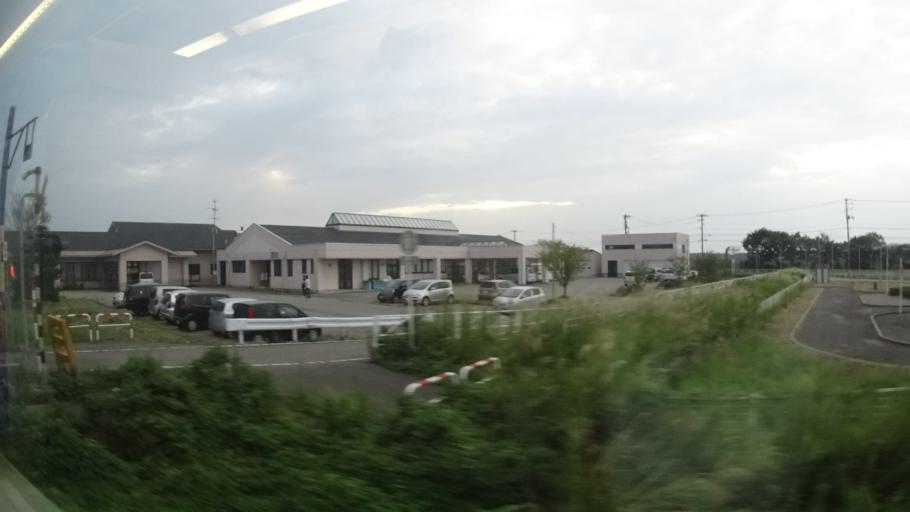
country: JP
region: Niigata
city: Murakami
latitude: 38.1773
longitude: 139.4595
